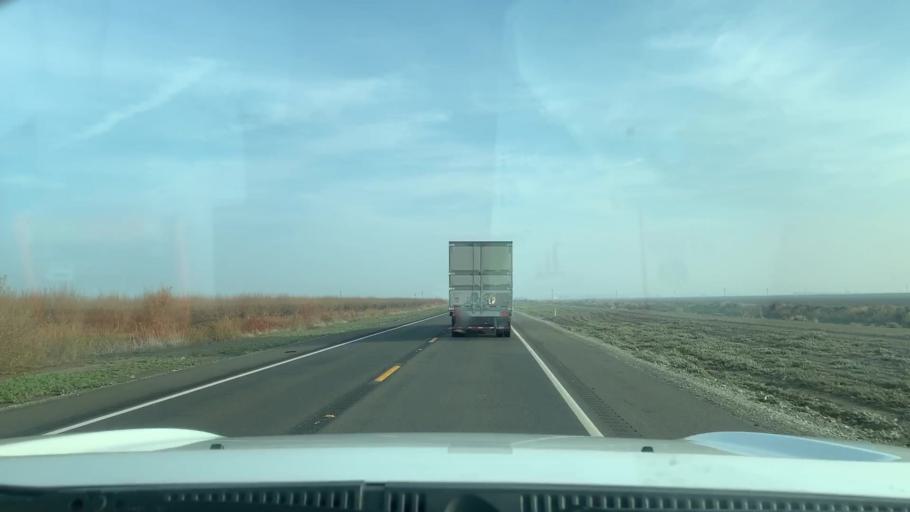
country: US
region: California
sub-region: Kings County
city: Stratford
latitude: 36.1628
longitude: -119.8494
